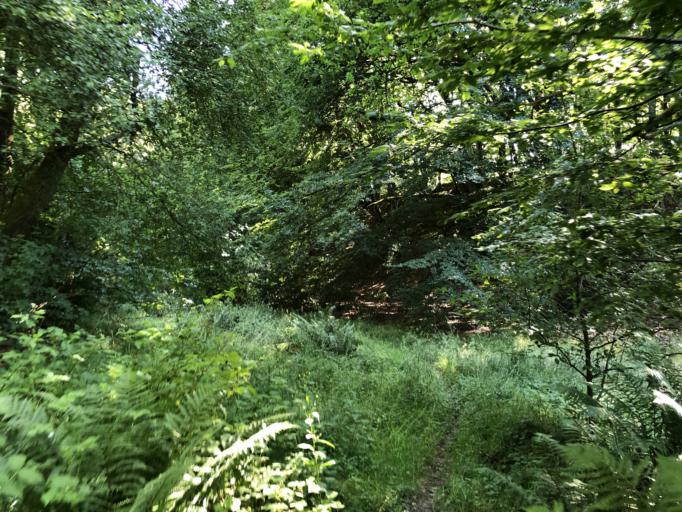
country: DK
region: Central Jutland
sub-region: Viborg Kommune
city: Stoholm
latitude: 56.4445
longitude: 9.1388
